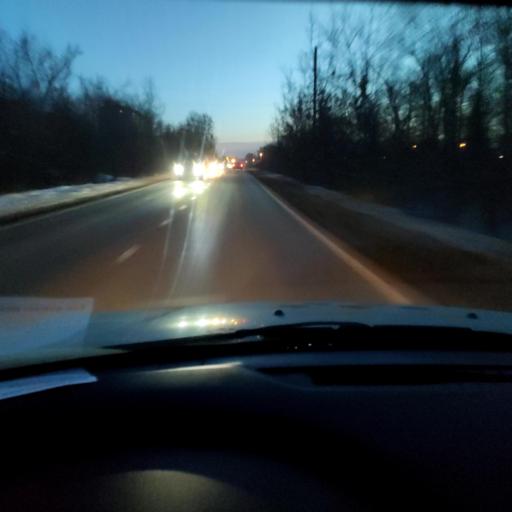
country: RU
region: Samara
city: Tol'yatti
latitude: 53.5464
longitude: 49.3934
